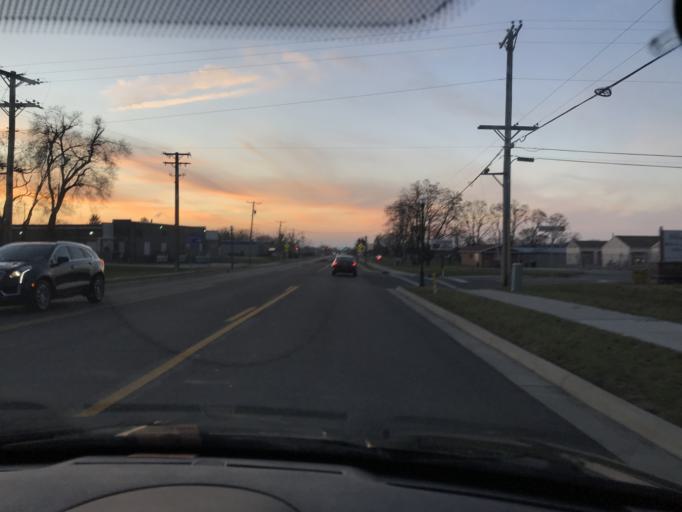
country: US
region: Ohio
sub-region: Champaign County
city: Urbana
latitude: 40.1064
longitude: -83.7242
